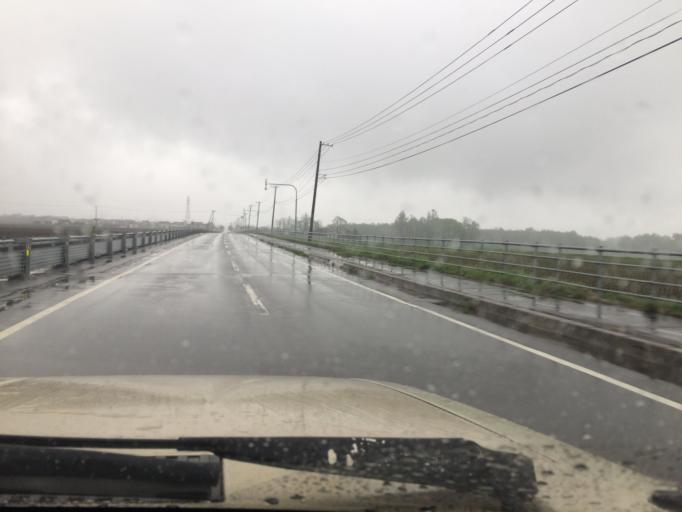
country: JP
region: Hokkaido
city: Obihiro
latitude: 42.8930
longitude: 143.0412
